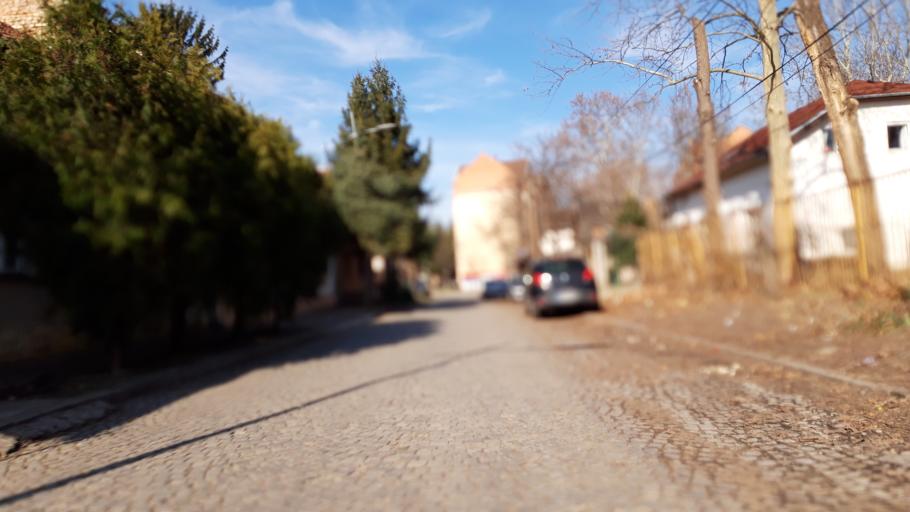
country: RS
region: Autonomna Pokrajina Vojvodina
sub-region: Juznobacki Okrug
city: Novi Sad
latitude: 45.2615
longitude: 19.8264
